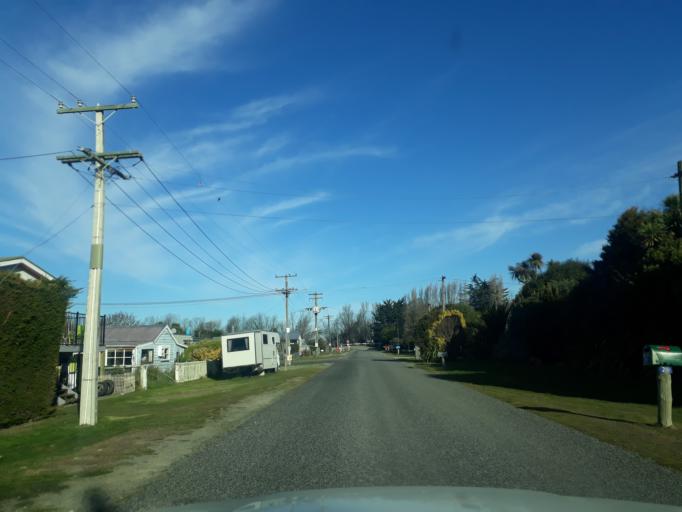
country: NZ
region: Canterbury
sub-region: Timaru District
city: Timaru
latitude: -44.2750
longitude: 171.3480
